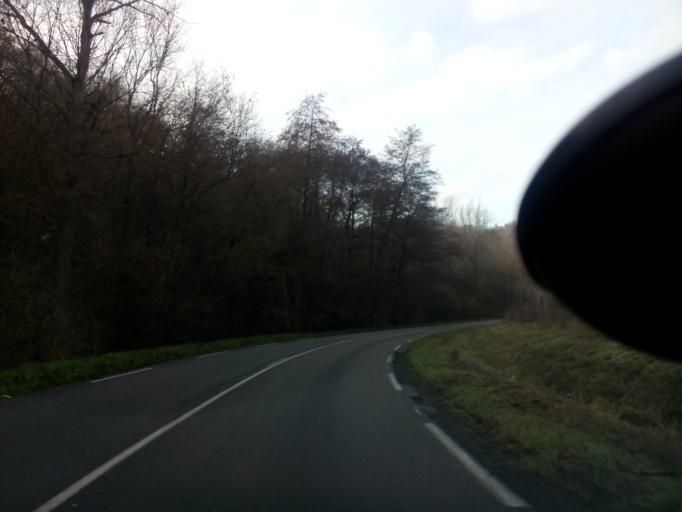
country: FR
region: Rhone-Alpes
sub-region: Departement de la Loire
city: Saint-Pierre-de-Boeuf
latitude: 45.3786
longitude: 4.7208
